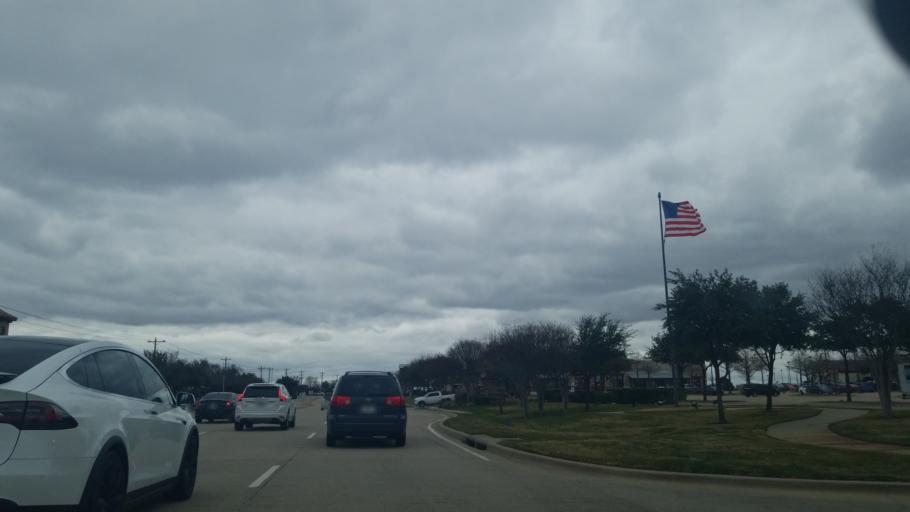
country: US
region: Texas
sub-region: Denton County
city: Double Oak
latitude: 33.0679
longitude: -97.0816
